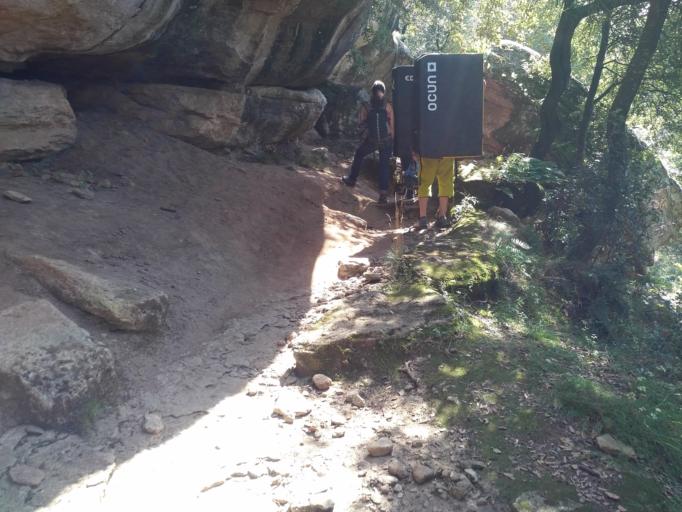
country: ES
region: Catalonia
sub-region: Provincia de Barcelona
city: Taradell
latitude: 41.8643
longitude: 2.3122
